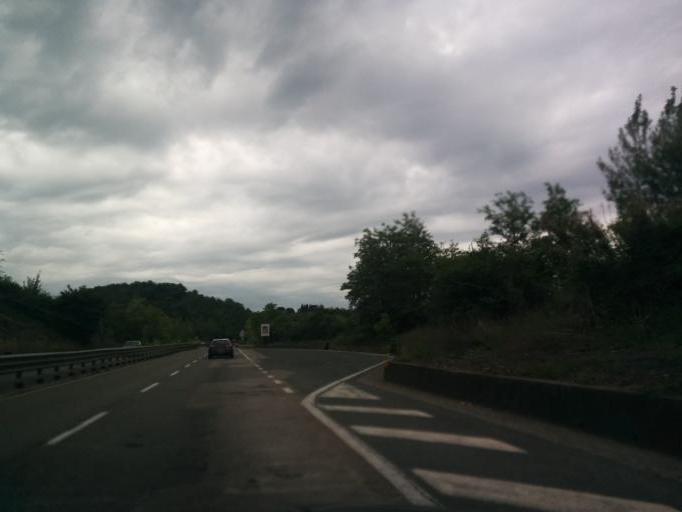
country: IT
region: Tuscany
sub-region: Provincia di Siena
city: Belverde
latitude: 43.3680
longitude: 11.2937
